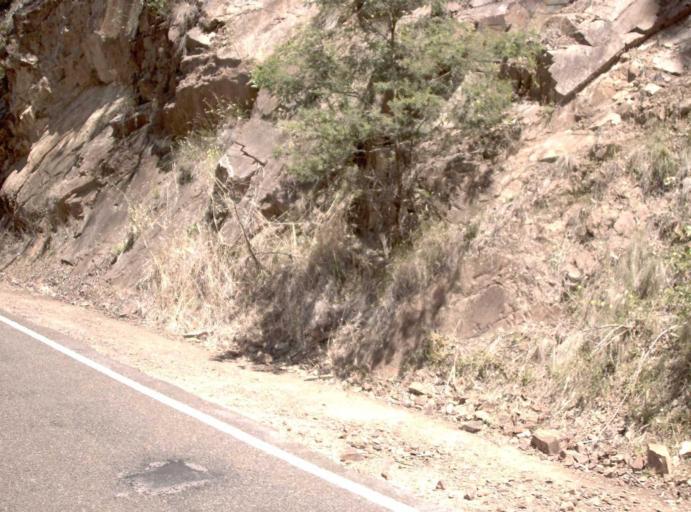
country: AU
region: Victoria
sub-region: East Gippsland
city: Bairnsdale
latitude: -37.4777
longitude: 147.8307
